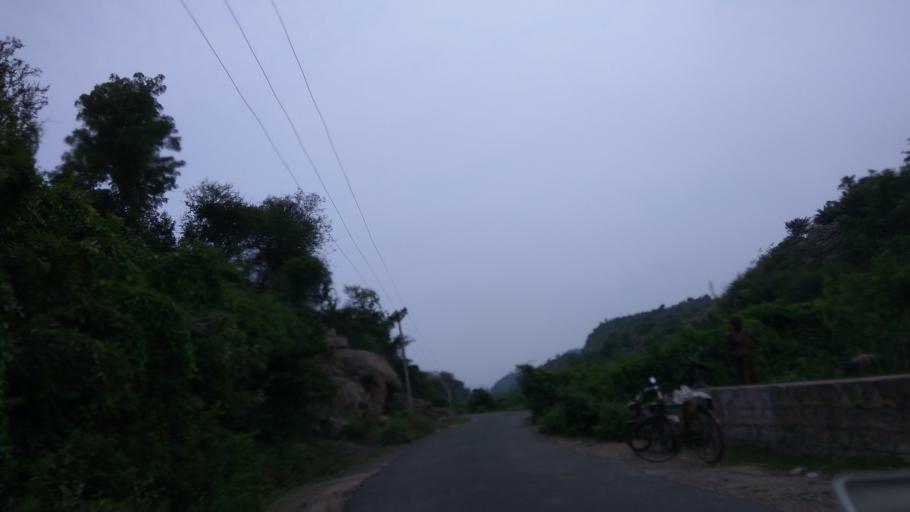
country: IN
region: Tamil Nadu
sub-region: Dharmapuri
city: Dharmapuri
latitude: 12.0193
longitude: 78.1214
